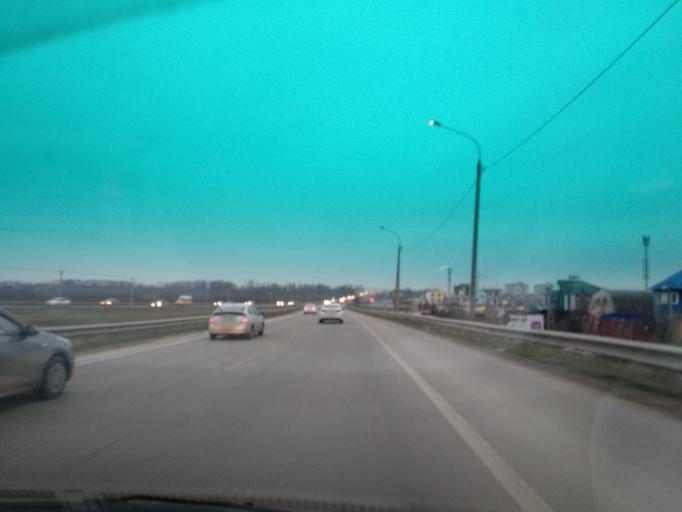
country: RU
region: Krasnodarskiy
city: Pashkovskiy
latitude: 45.0532
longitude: 39.1304
